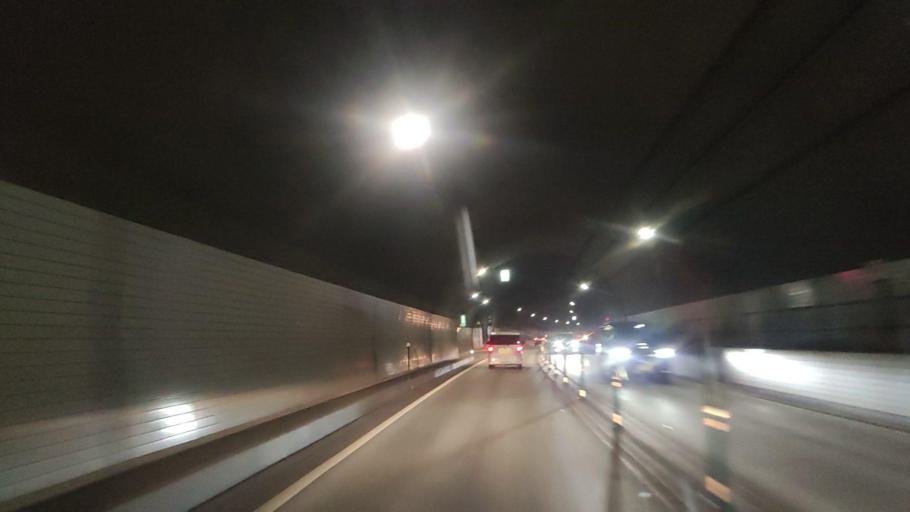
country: JP
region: Gifu
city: Takayama
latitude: 36.1758
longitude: 137.2249
